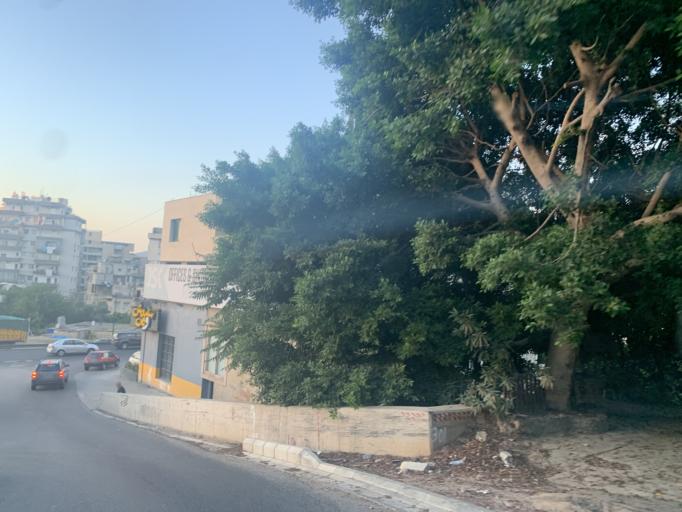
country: LB
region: Mont-Liban
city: Djounie
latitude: 33.9772
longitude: 35.6292
